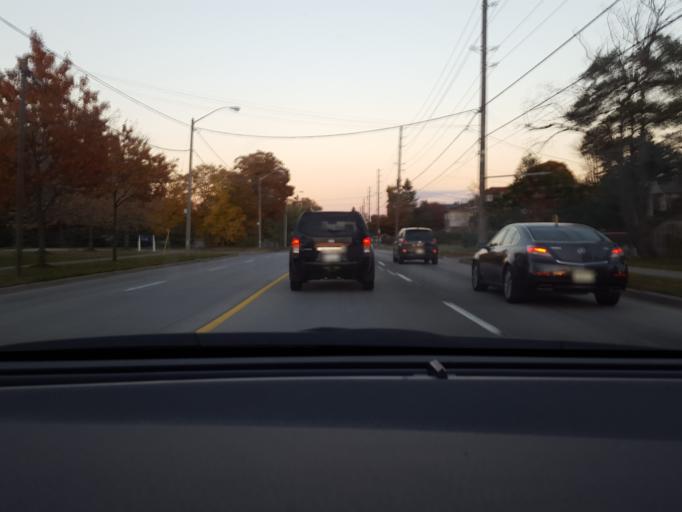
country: CA
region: Ontario
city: Scarborough
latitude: 43.7869
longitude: -79.1873
